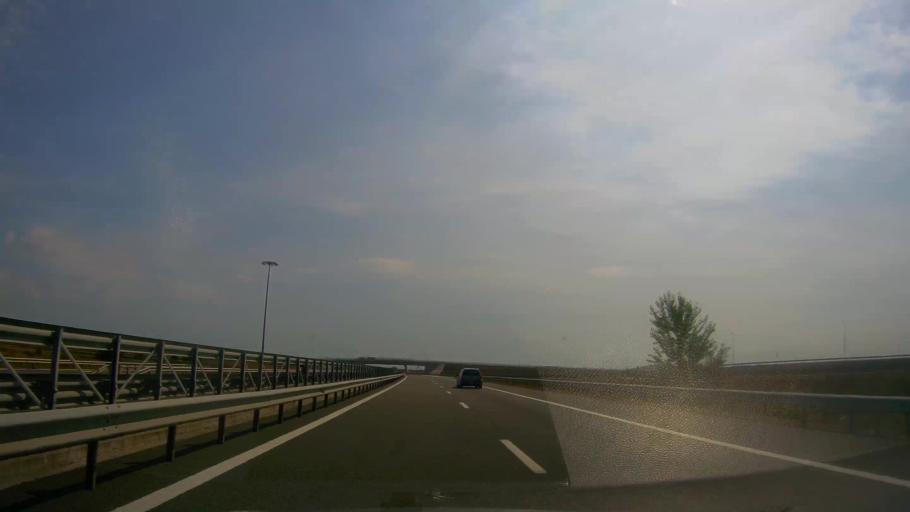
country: RO
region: Cluj
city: Turda
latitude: 46.5272
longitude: 23.7921
